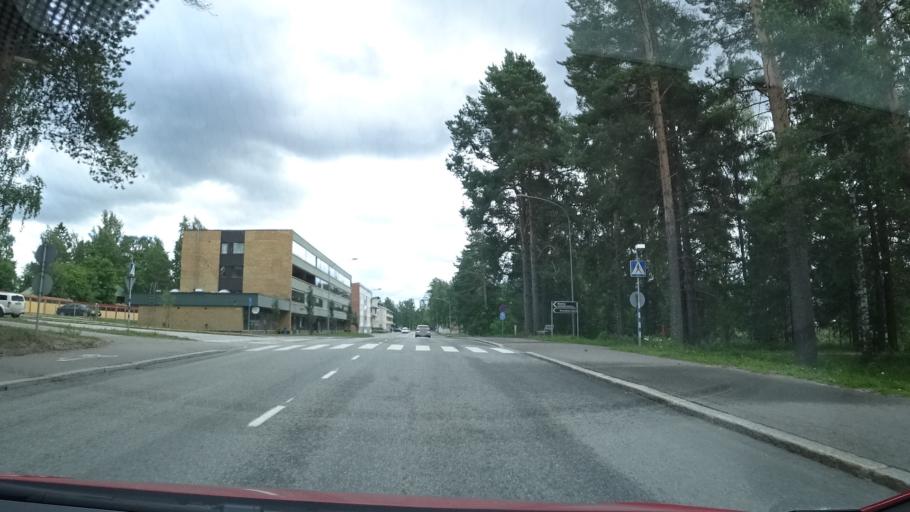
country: FI
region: North Karelia
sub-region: Pielisen Karjala
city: Nurmes
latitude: 63.5439
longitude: 29.1325
